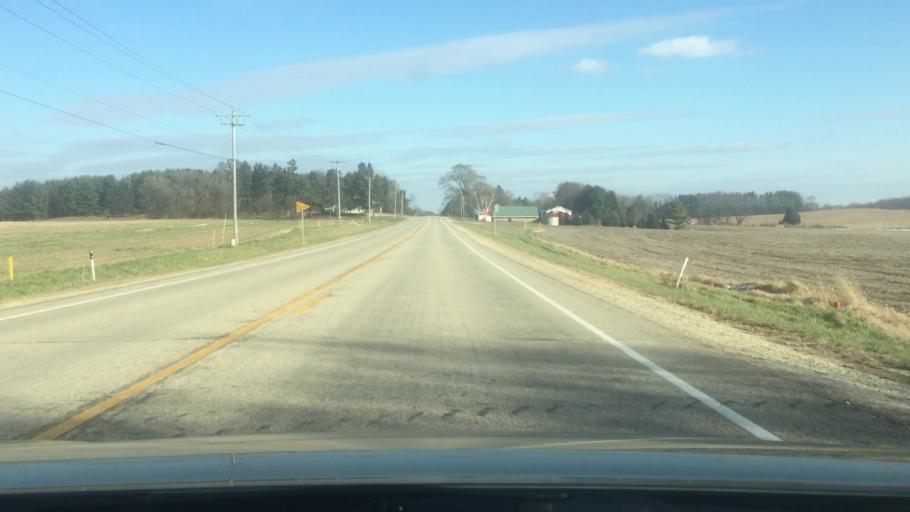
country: US
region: Wisconsin
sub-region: Jefferson County
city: Fort Atkinson
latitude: 42.9391
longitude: -88.7731
